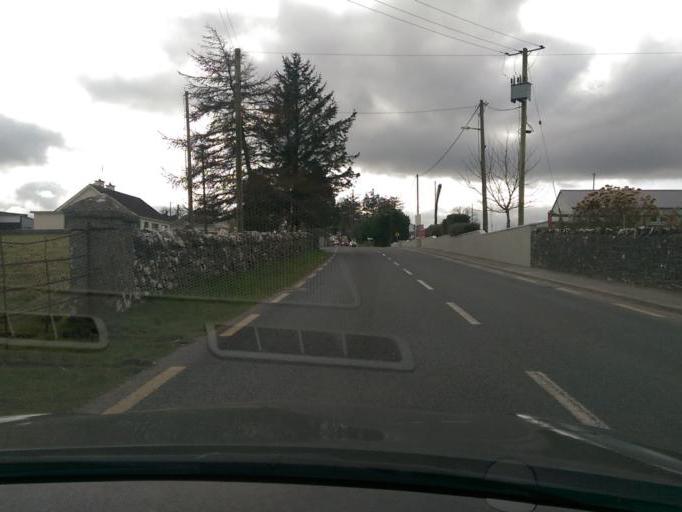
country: IE
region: Connaught
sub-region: County Galway
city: Ballinasloe
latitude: 53.3305
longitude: -8.4035
